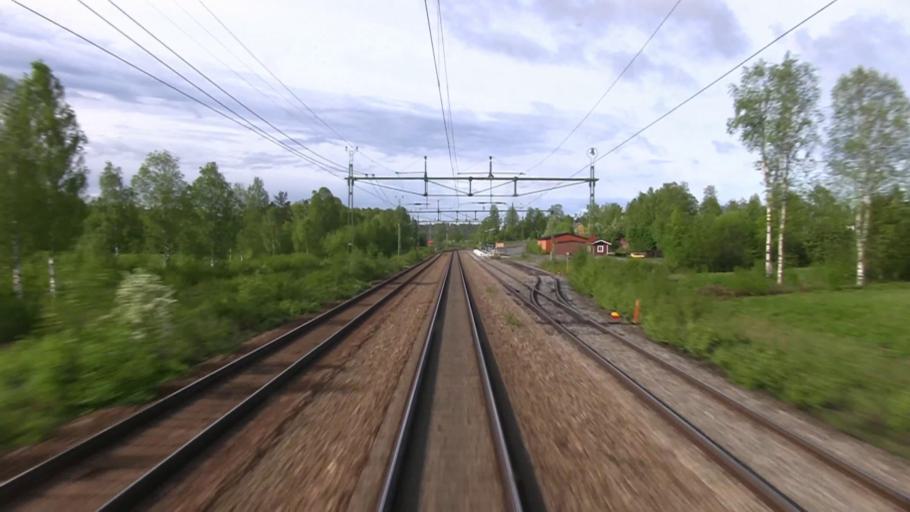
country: SE
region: Vaesterbotten
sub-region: Vindelns Kommun
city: Vindeln
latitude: 64.0993
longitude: 19.6772
